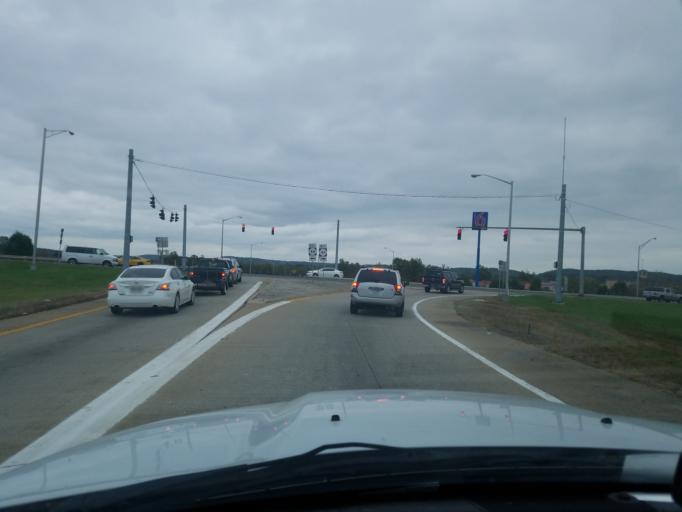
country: US
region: Kentucky
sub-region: Bullitt County
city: Shepherdsville
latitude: 37.9924
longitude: -85.7059
